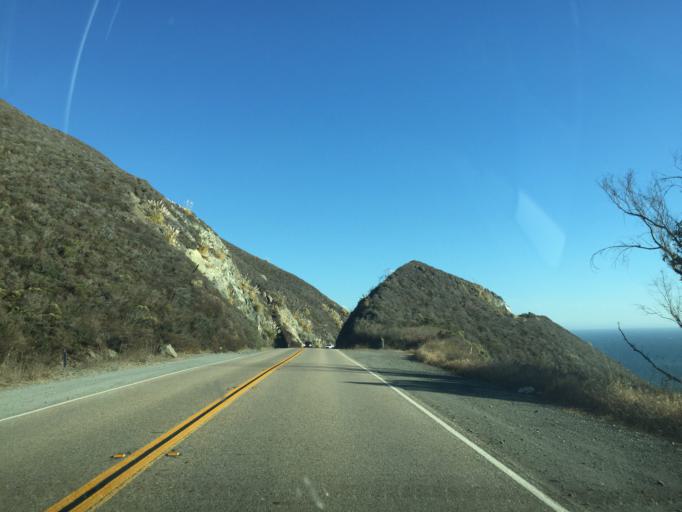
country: US
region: California
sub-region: Monterey County
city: King City
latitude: 35.8687
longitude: -121.4370
